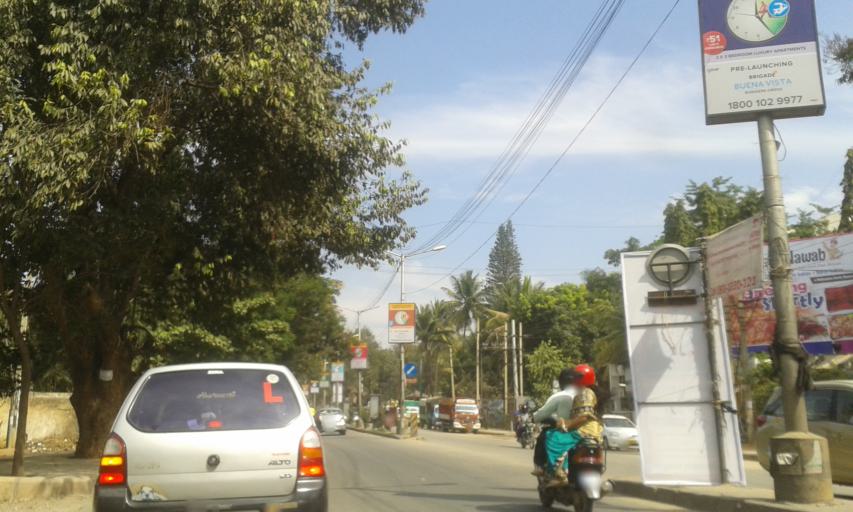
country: IN
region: Karnataka
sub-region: Bangalore Rural
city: Hoskote
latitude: 12.9661
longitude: 77.7490
